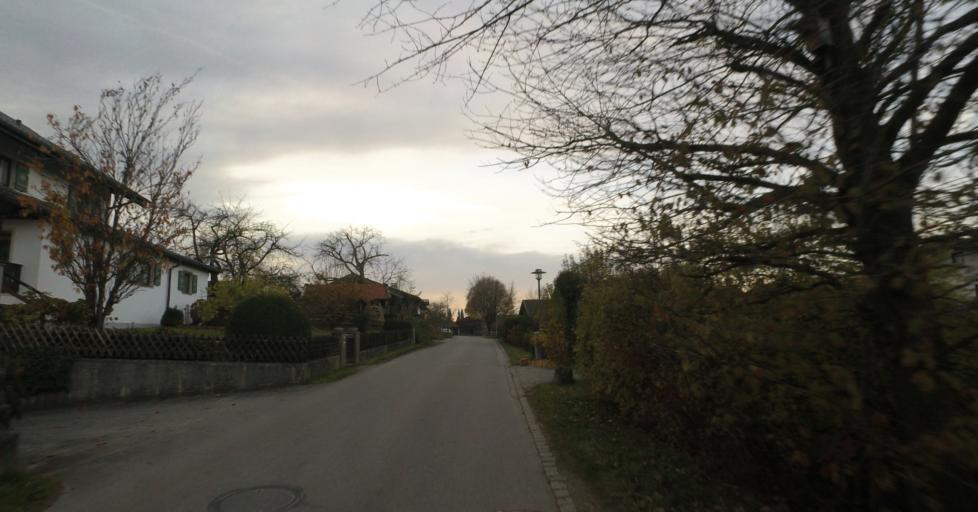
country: DE
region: Bavaria
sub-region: Upper Bavaria
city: Gstadt am Chiemsee
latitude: 47.8911
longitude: 12.4024
